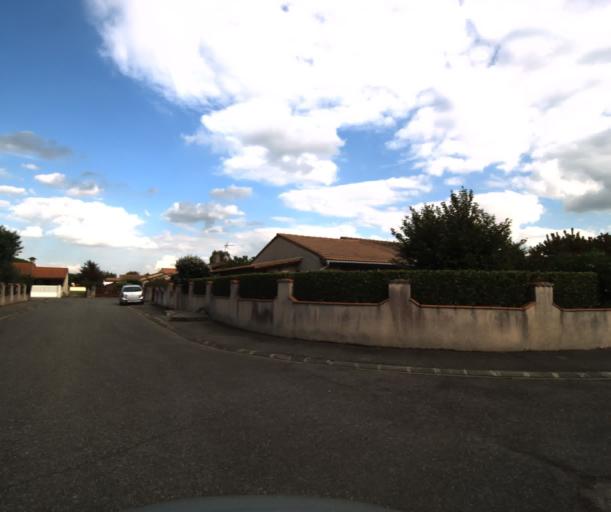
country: FR
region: Midi-Pyrenees
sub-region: Departement de la Haute-Garonne
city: Labarthe-sur-Leze
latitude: 43.4446
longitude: 1.3932
